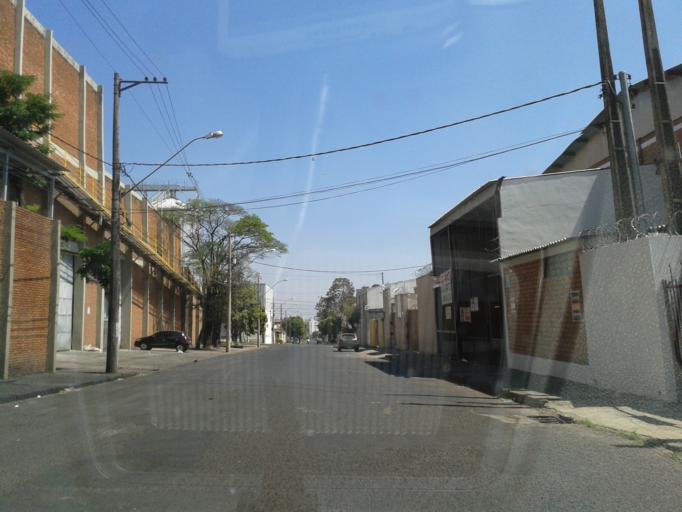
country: BR
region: Minas Gerais
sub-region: Uberlandia
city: Uberlandia
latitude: -18.8972
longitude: -48.2483
